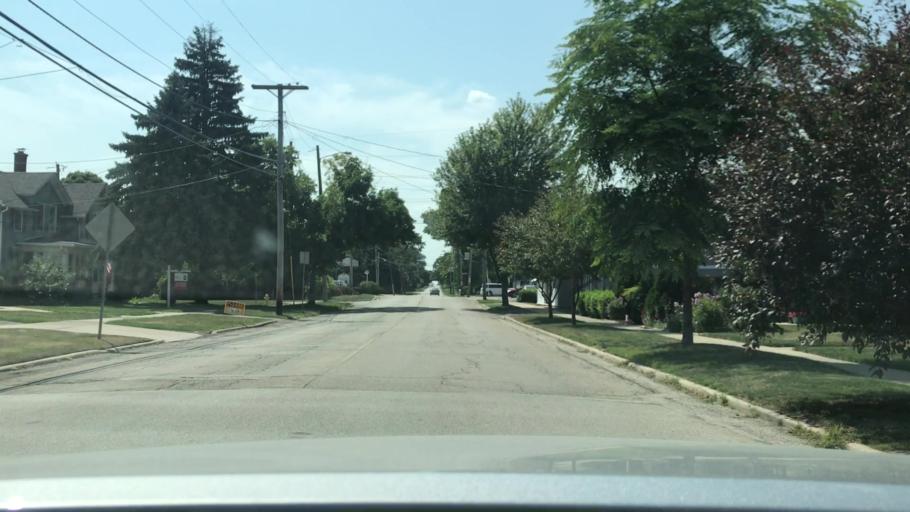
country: US
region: Illinois
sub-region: Kane County
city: Batavia
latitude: 41.8469
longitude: -88.3184
